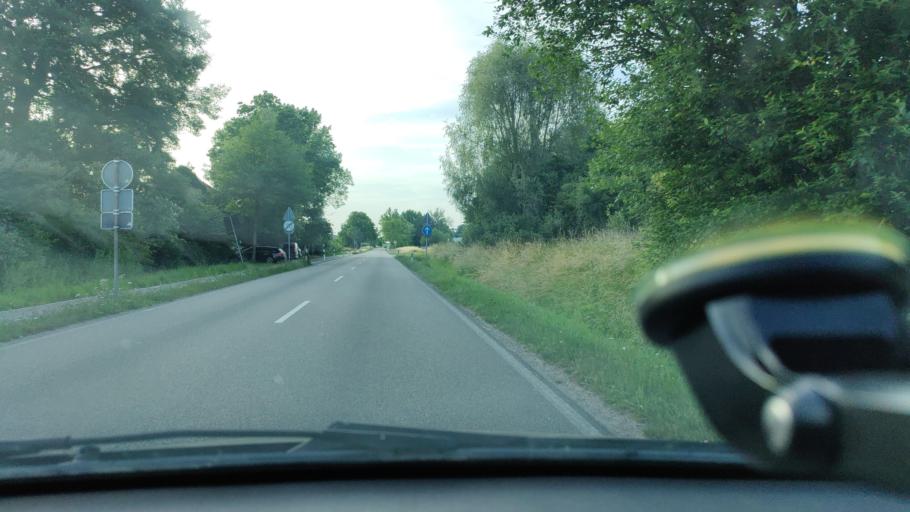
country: DE
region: North Rhine-Westphalia
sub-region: Regierungsbezirk Munster
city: Coesfeld
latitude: 52.0117
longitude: 7.1895
